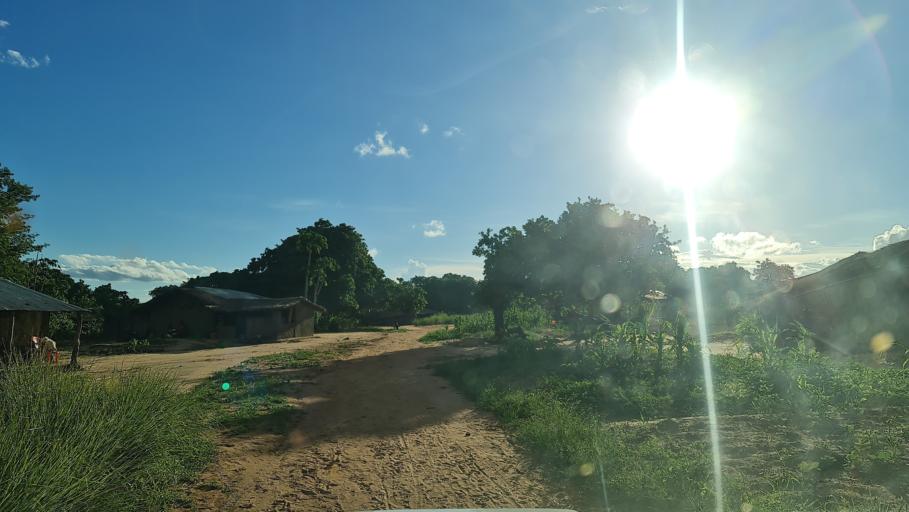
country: MZ
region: Nampula
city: Ilha de Mocambique
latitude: -14.9439
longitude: 40.1641
